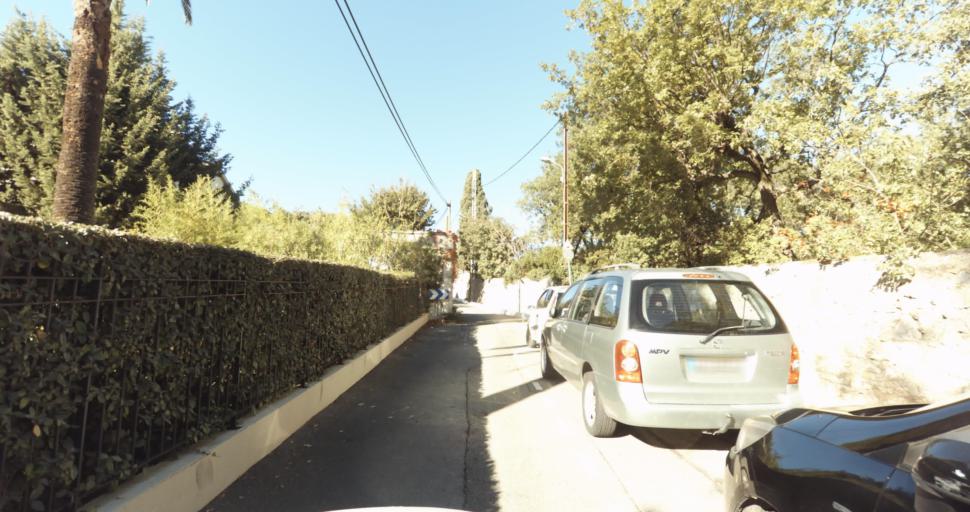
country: FR
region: Provence-Alpes-Cote d'Azur
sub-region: Departement des Alpes-Maritimes
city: Vence
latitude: 43.7216
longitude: 7.1046
